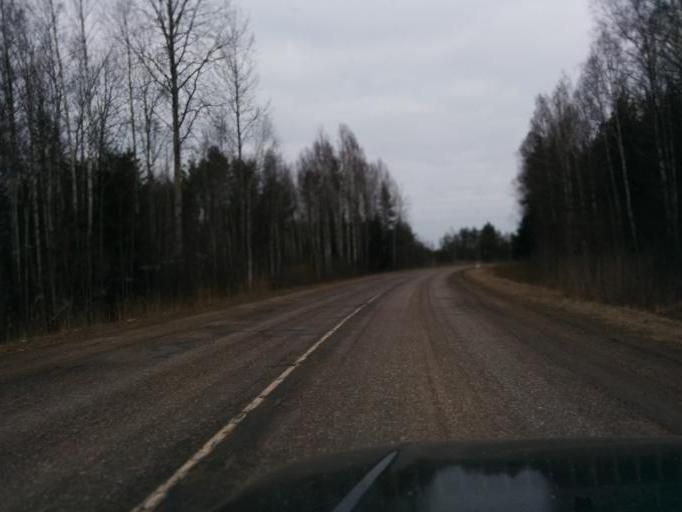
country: LV
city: Tireli
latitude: 56.8576
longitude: 23.5357
